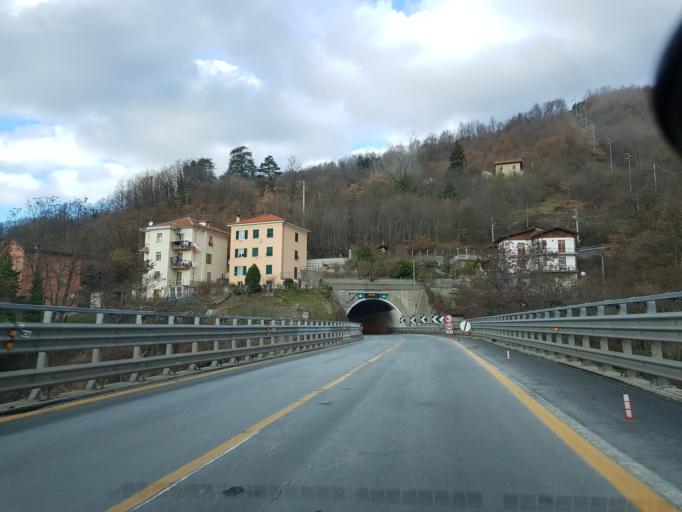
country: IT
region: Liguria
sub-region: Provincia di Genova
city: Ronco Scrivia
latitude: 44.6137
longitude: 8.9565
